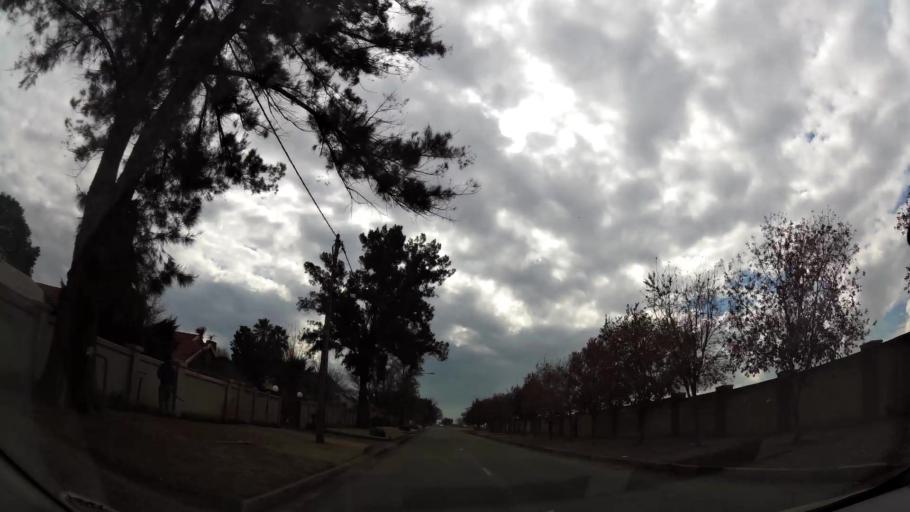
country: ZA
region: Gauteng
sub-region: Sedibeng District Municipality
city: Vereeniging
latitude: -26.6475
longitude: 27.9889
